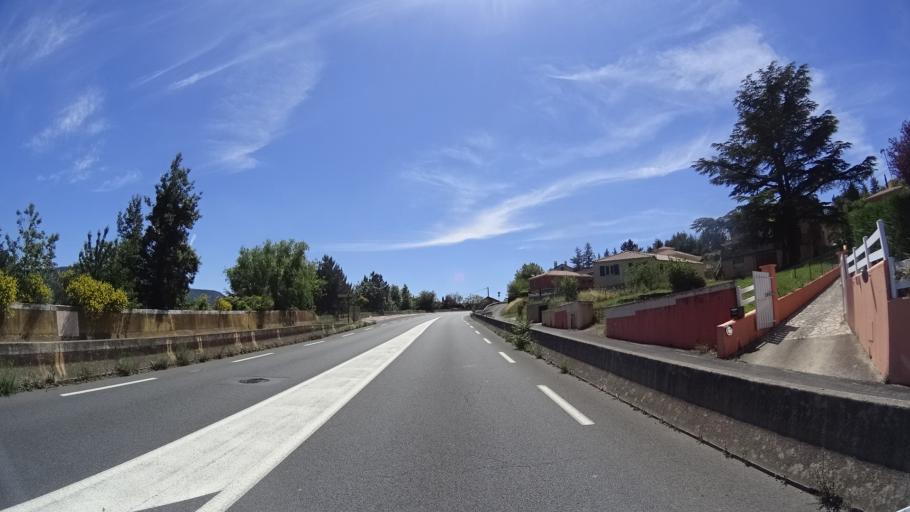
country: FR
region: Midi-Pyrenees
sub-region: Departement de l'Aveyron
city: Millau
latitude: 44.1146
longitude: 3.0803
